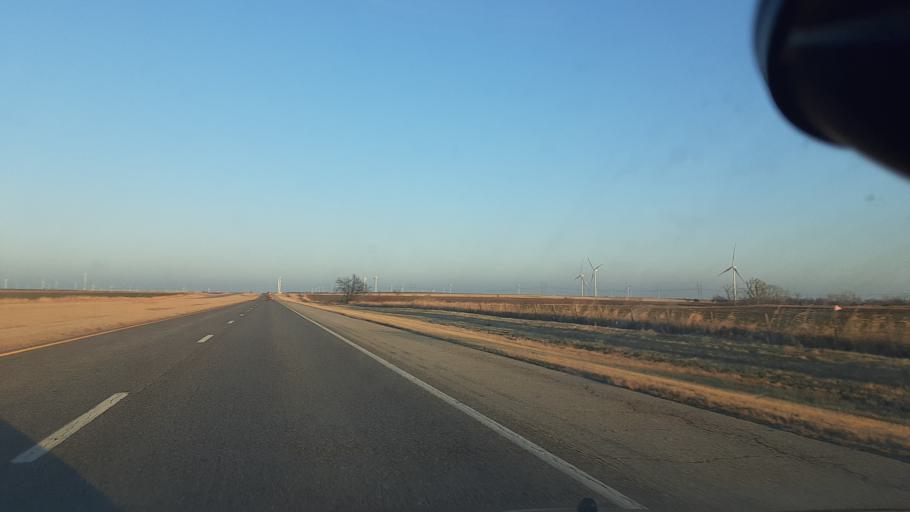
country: US
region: Oklahoma
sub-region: Noble County
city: Perry
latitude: 36.3975
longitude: -97.4944
